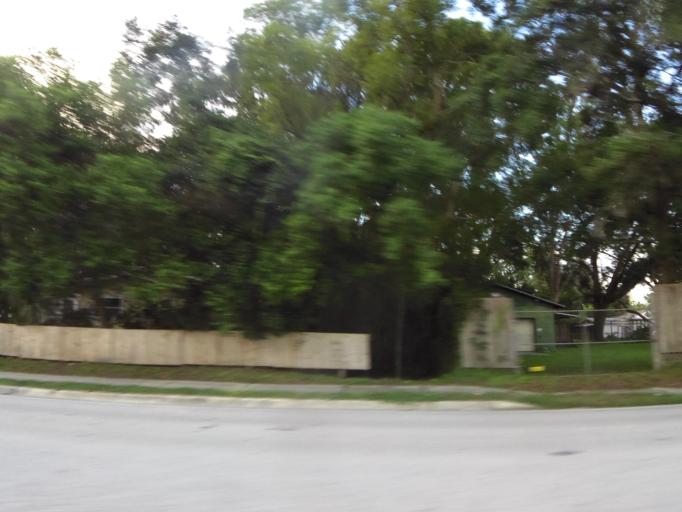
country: US
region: Florida
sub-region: Duval County
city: Jacksonville
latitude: 30.2644
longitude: -81.5966
